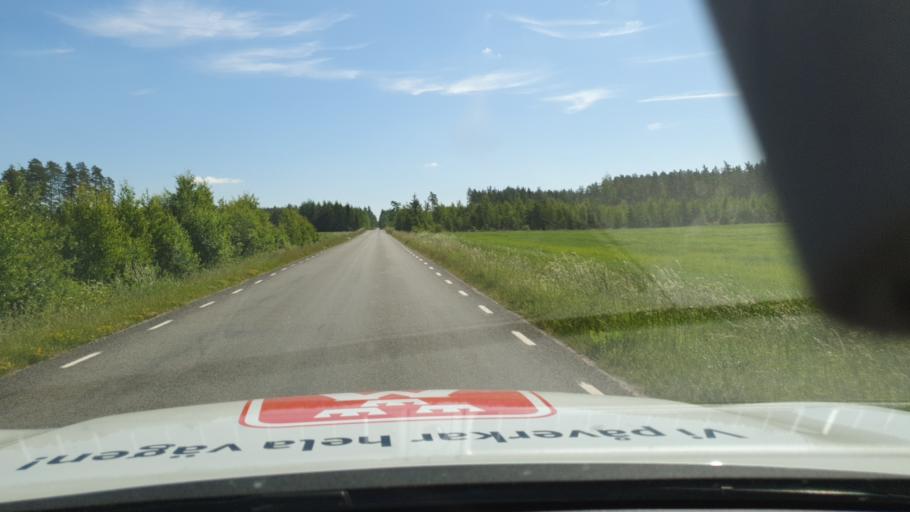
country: SE
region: Vaestra Goetaland
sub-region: Skovde Kommun
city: Skultorp
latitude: 58.2592
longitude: 13.8715
